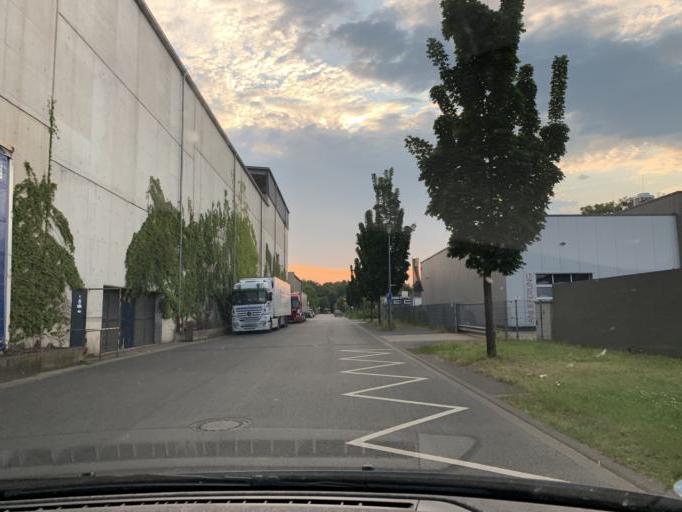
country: DE
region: North Rhine-Westphalia
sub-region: Regierungsbezirk Dusseldorf
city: Dusseldorf
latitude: 51.2224
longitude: 6.7402
